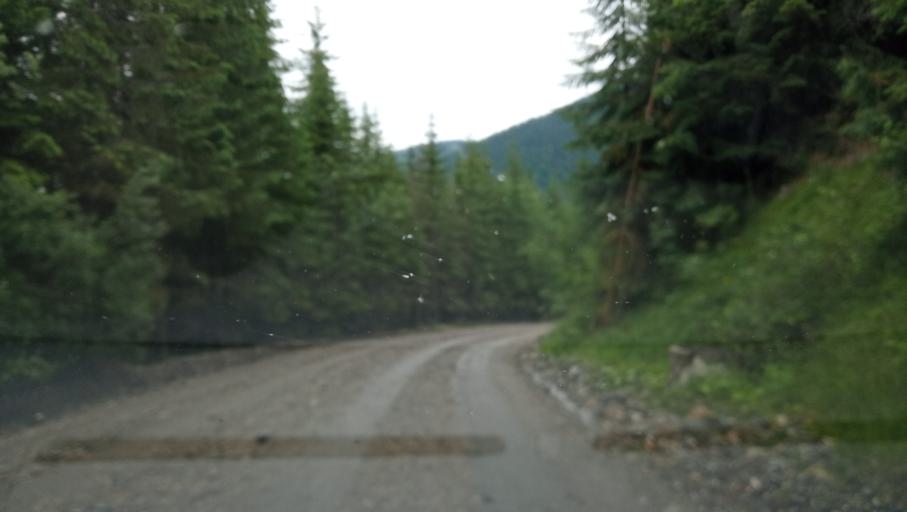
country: RO
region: Hunedoara
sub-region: Oras Petrila
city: Petrila
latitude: 45.4036
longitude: 23.5678
